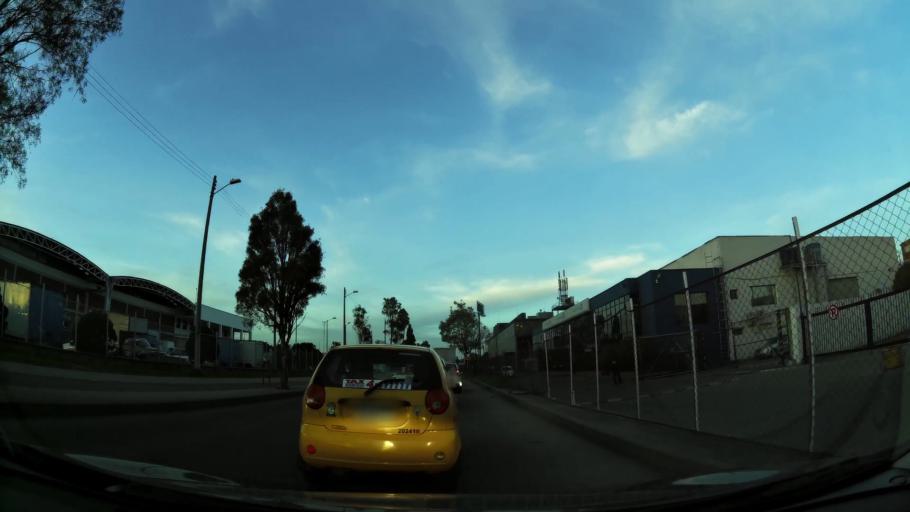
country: CO
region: Cundinamarca
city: Funza
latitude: 4.6879
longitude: -74.1325
